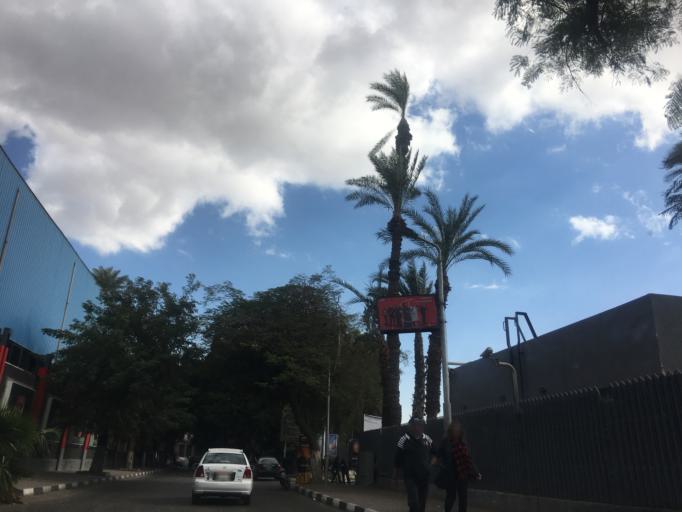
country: EG
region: Muhafazat al Qahirah
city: Cairo
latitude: 30.0438
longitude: 31.2229
